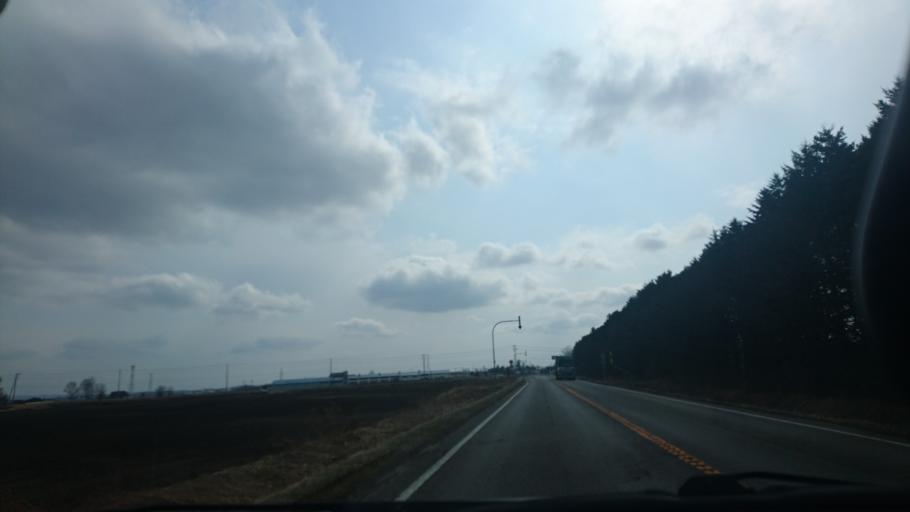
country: JP
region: Hokkaido
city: Otofuke
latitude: 43.1571
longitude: 143.2449
